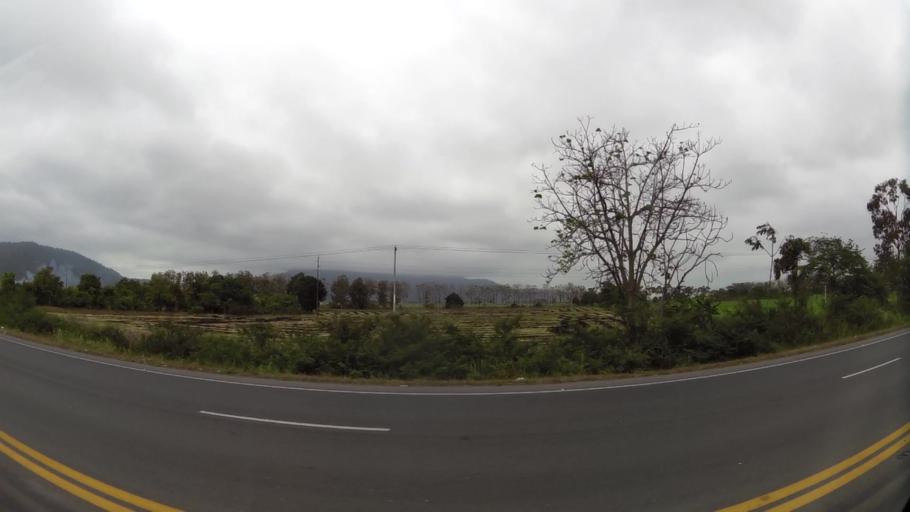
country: EC
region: Guayas
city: Naranjal
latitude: -2.4831
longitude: -79.6163
